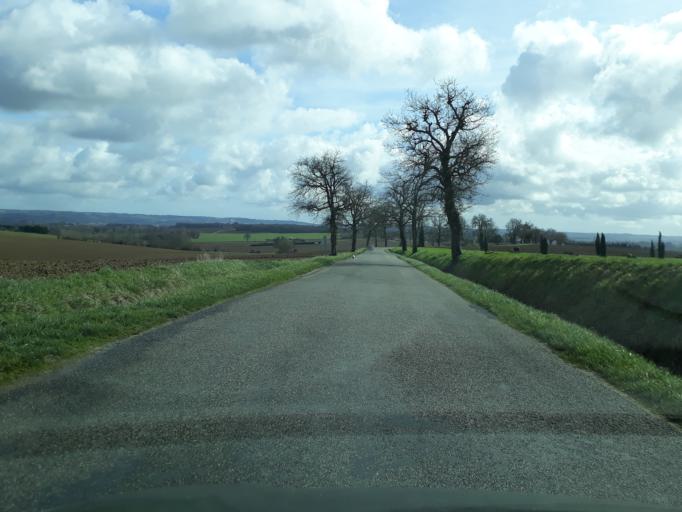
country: FR
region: Midi-Pyrenees
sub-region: Departement du Gers
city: Gimont
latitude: 43.6390
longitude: 1.0025
